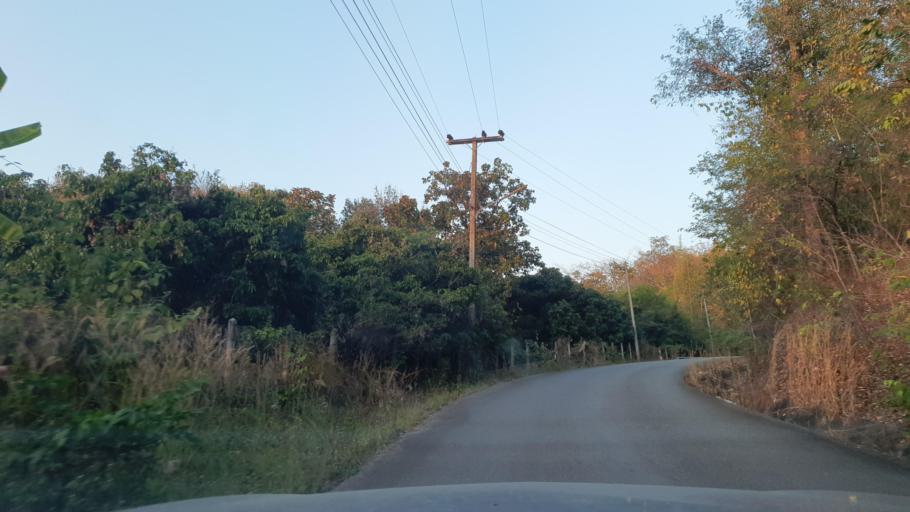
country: TH
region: Chiang Mai
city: Mae Wang
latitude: 18.6873
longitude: 98.8144
